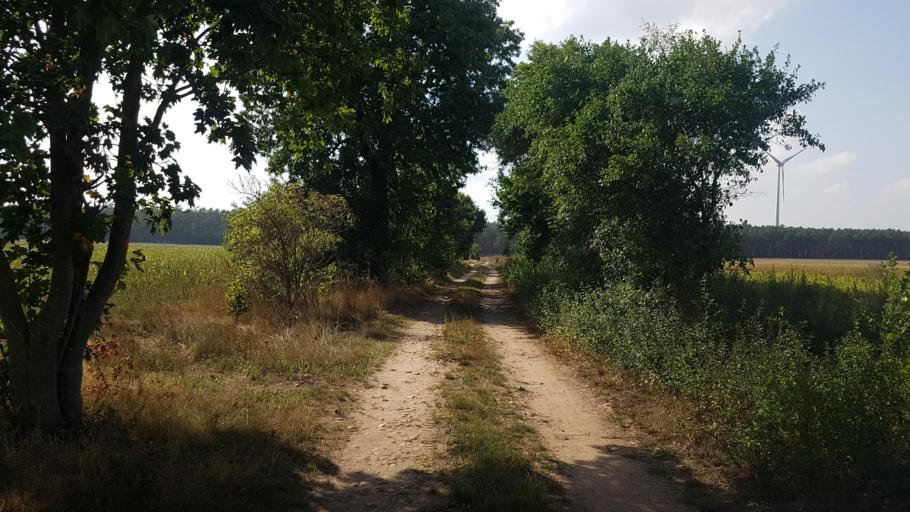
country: DE
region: Brandenburg
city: Dahme
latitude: 51.9656
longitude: 13.4317
